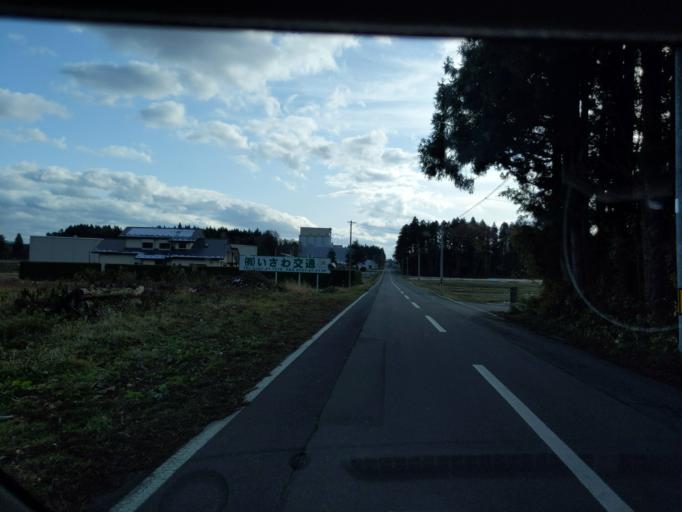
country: JP
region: Iwate
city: Mizusawa
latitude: 39.1082
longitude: 141.0820
